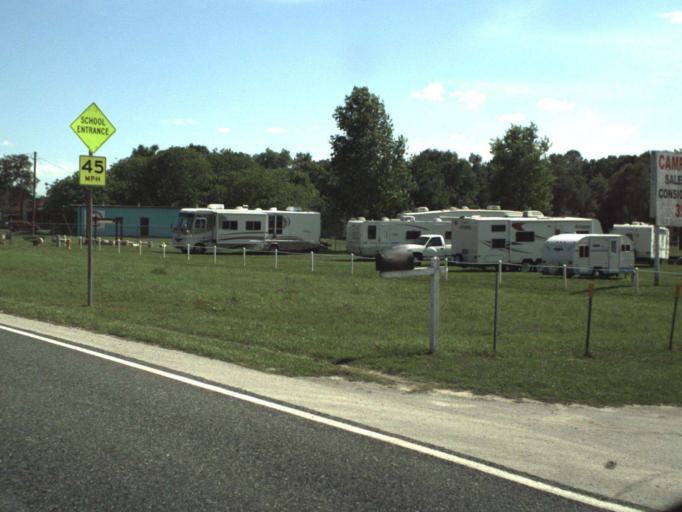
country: US
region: Florida
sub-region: Marion County
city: Belleview
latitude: 29.0861
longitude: -82.0800
